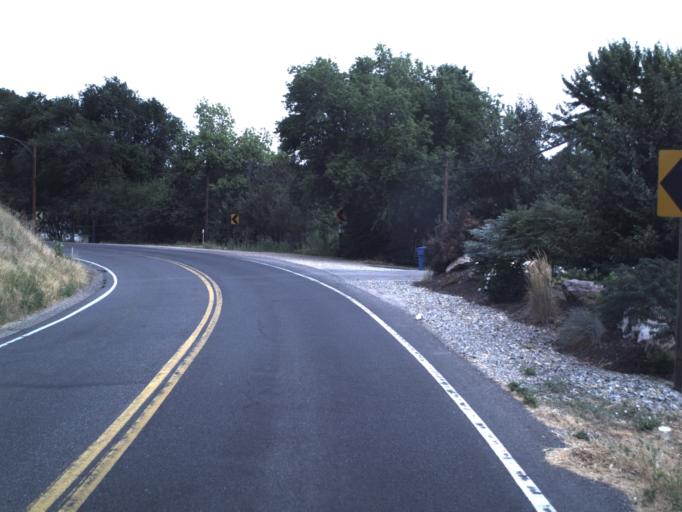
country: US
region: Utah
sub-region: Weber County
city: Riverdale
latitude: 41.1621
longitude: -112.0049
